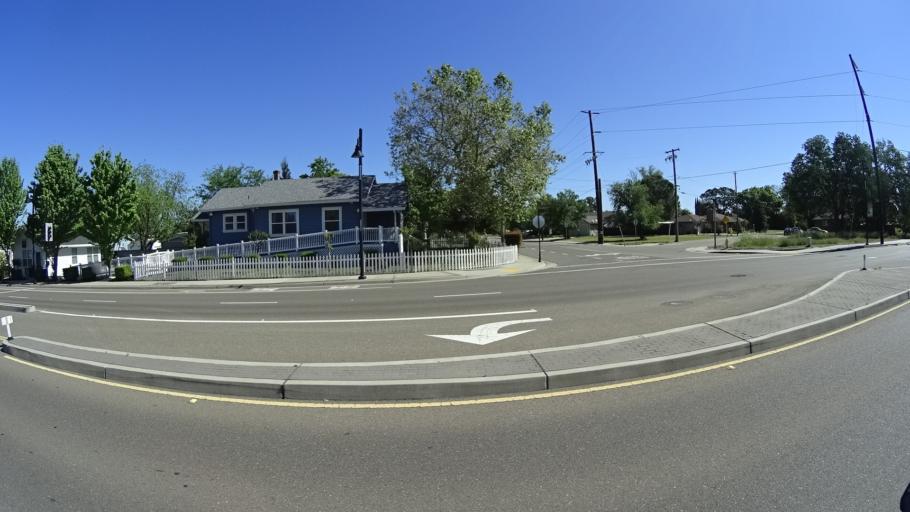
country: US
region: California
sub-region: Placer County
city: Rocklin
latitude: 38.7892
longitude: -121.2327
